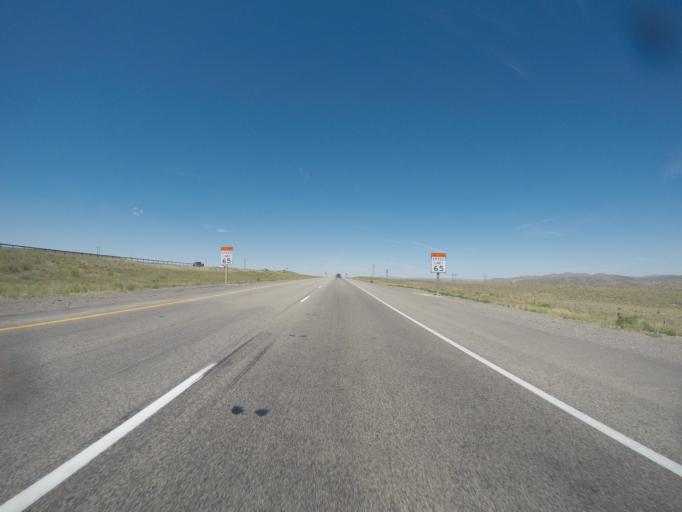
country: US
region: Wyoming
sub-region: Carbon County
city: Saratoga
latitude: 41.7421
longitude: -106.8434
